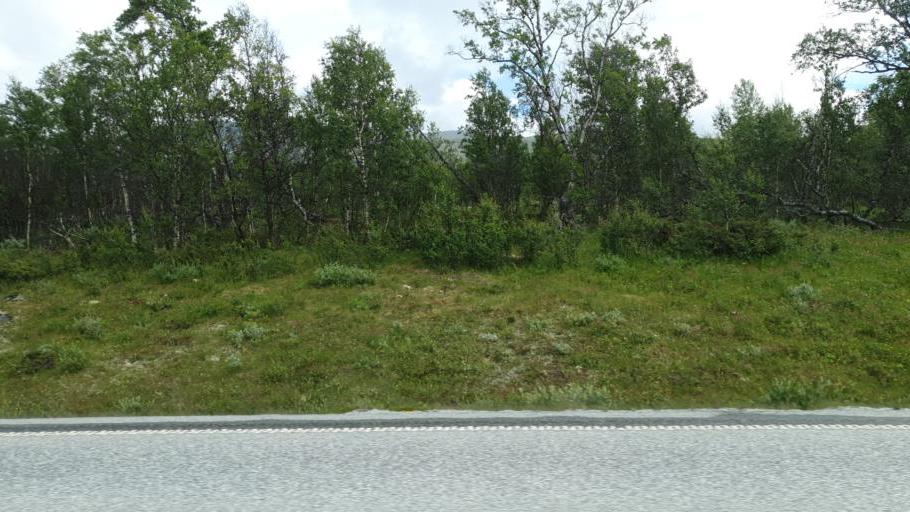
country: NO
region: Oppland
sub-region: Dovre
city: Dovre
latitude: 62.1302
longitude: 9.3092
